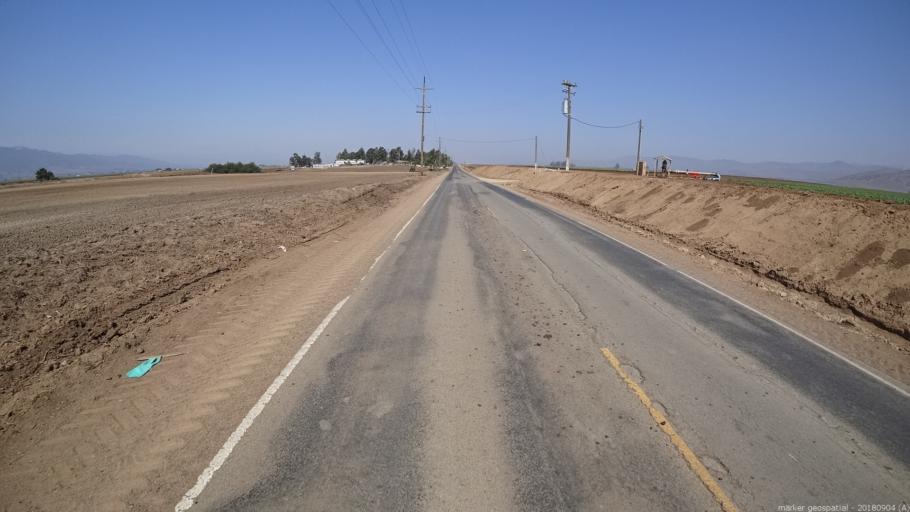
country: US
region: California
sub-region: Monterey County
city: Gonzales
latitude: 36.5437
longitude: -121.4680
